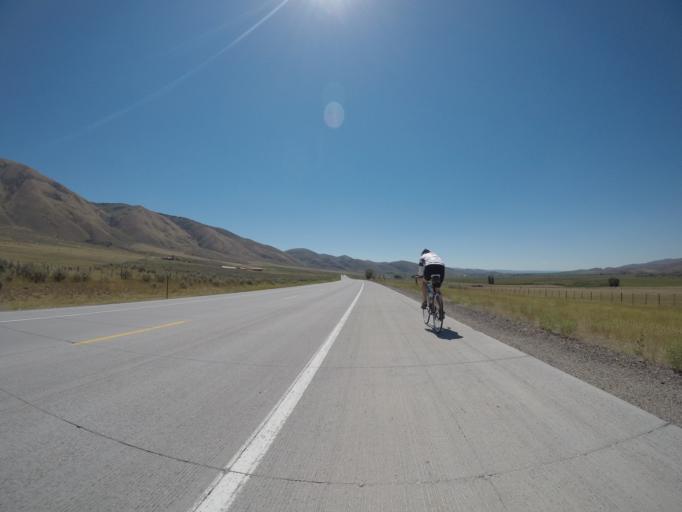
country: US
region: Idaho
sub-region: Bear Lake County
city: Montpelier
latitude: 42.1798
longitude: -111.0067
